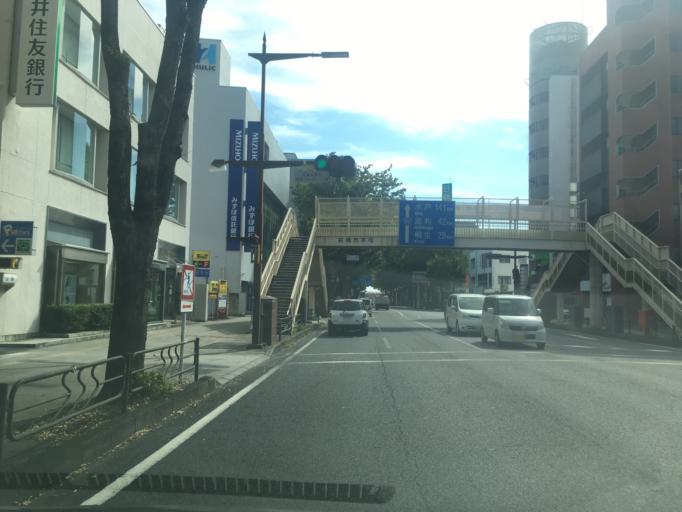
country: JP
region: Gunma
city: Maebashi-shi
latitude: 36.3906
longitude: 139.0688
